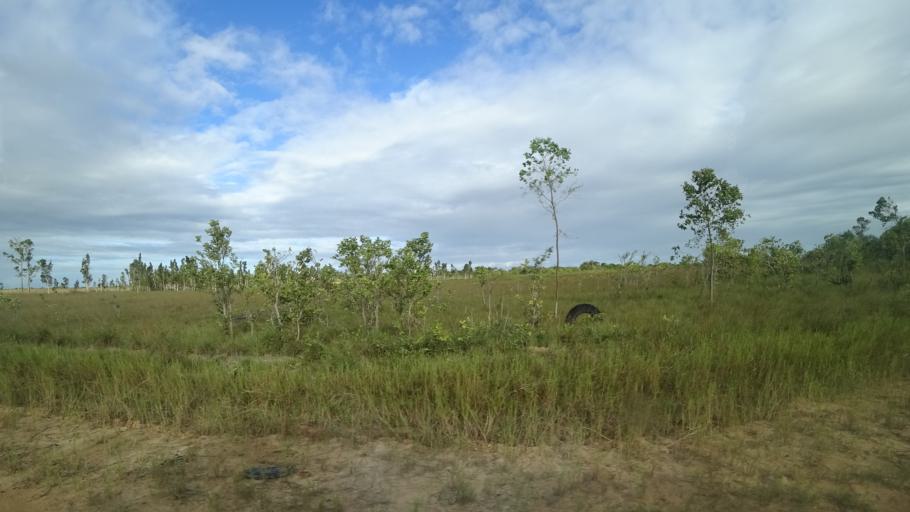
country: MZ
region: Sofala
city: Beira
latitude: -19.6801
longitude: 35.0580
